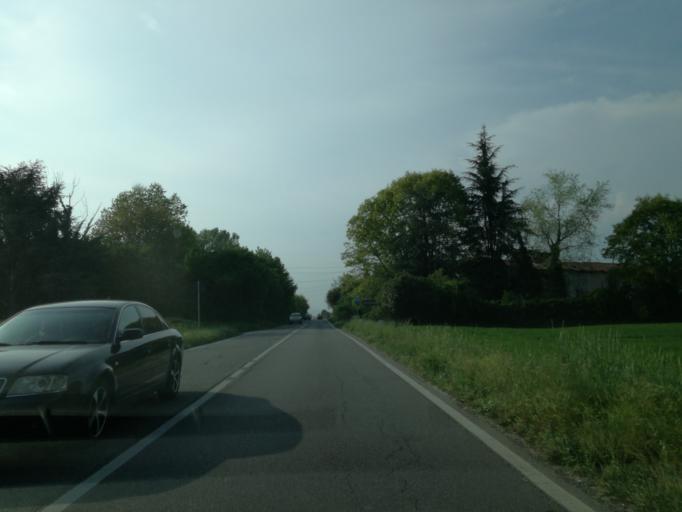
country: IT
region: Lombardy
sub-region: Provincia di Lecco
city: Verderio Superiore
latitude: 45.6575
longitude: 9.4562
